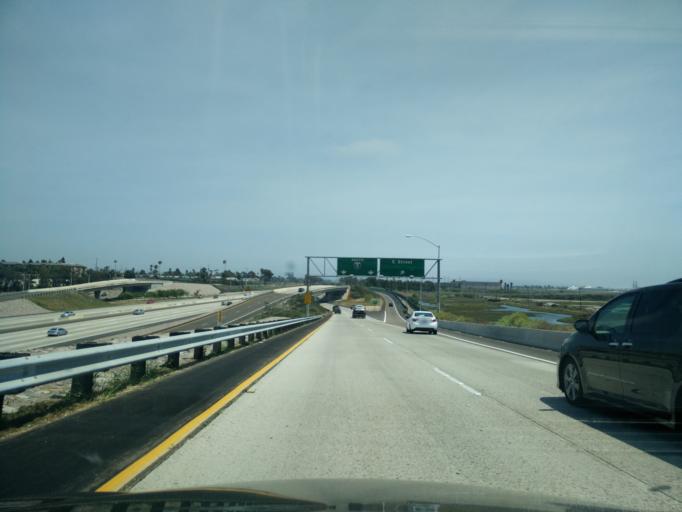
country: US
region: California
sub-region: San Diego County
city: Chula Vista
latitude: 32.6482
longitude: -117.1038
